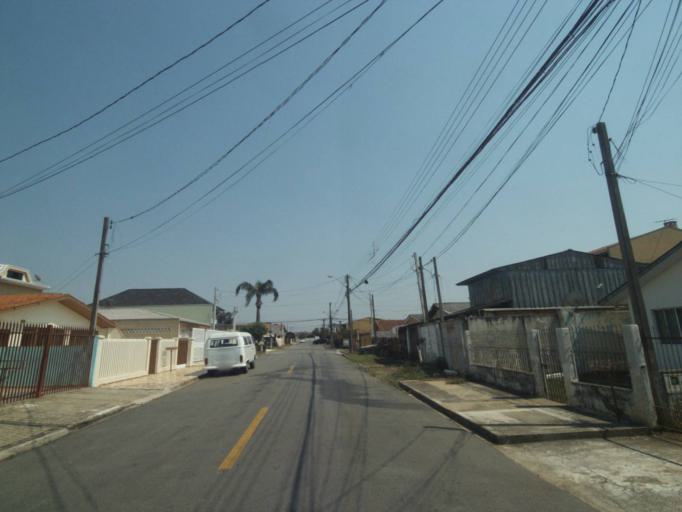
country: BR
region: Parana
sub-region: Sao Jose Dos Pinhais
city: Sao Jose dos Pinhais
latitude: -25.5132
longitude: -49.2771
